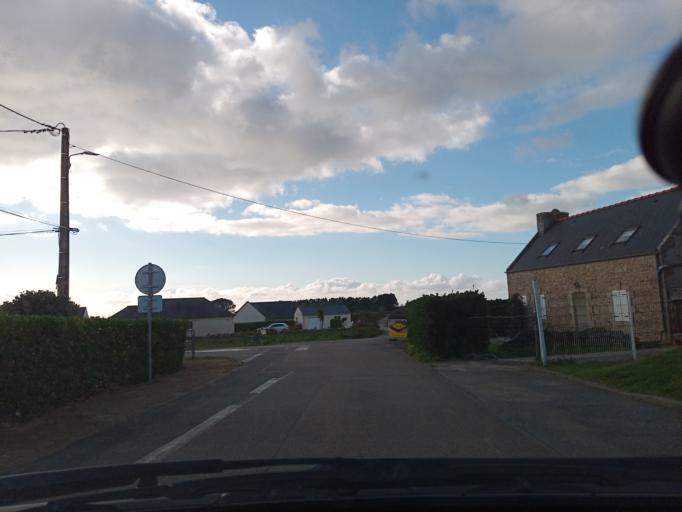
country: FR
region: Brittany
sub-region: Departement du Finistere
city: Plouhinec
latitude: 48.0168
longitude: -4.4923
